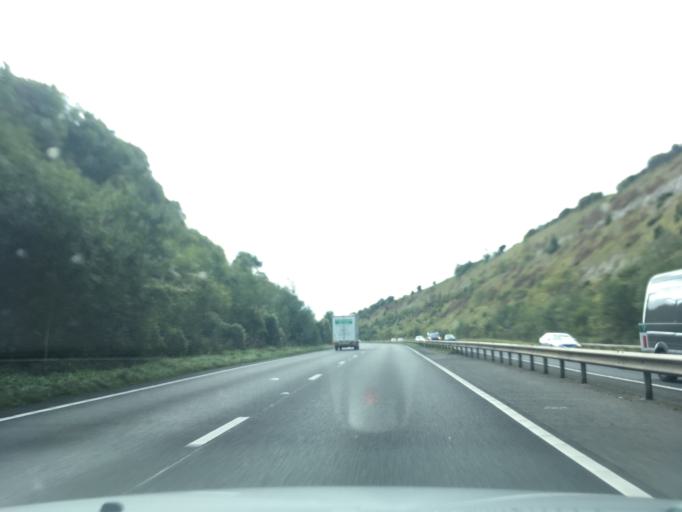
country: GB
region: England
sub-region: Hampshire
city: Petersfield
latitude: 50.9768
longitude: -0.9702
